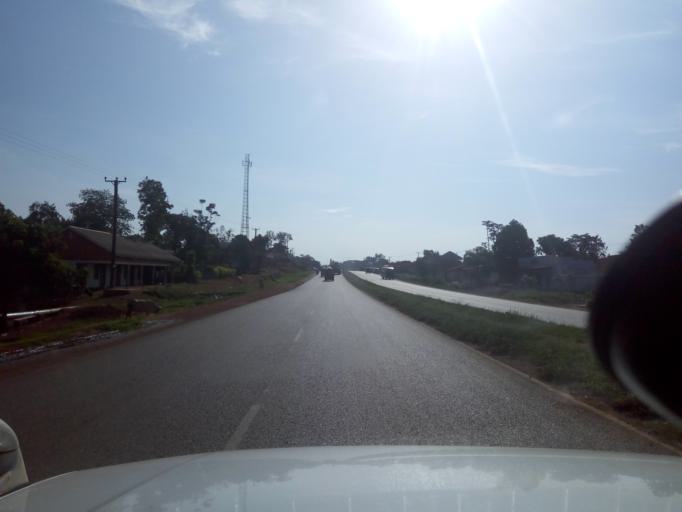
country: UG
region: Eastern Region
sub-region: Jinja District
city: Bugembe
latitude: 0.4750
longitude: 33.2618
